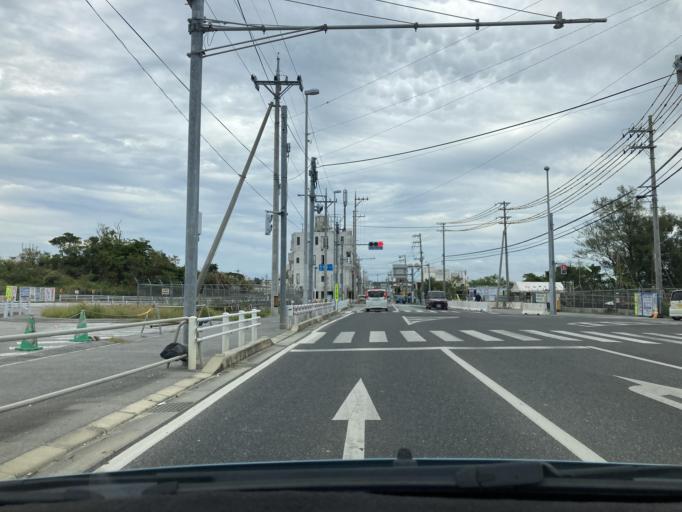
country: JP
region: Okinawa
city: Okinawa
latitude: 26.3827
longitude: 127.7453
